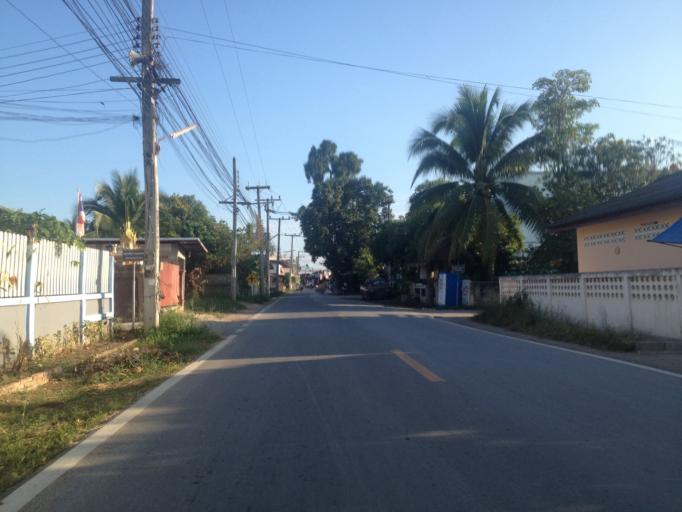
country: TH
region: Chiang Mai
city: San Pa Tong
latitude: 18.5665
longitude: 98.8702
